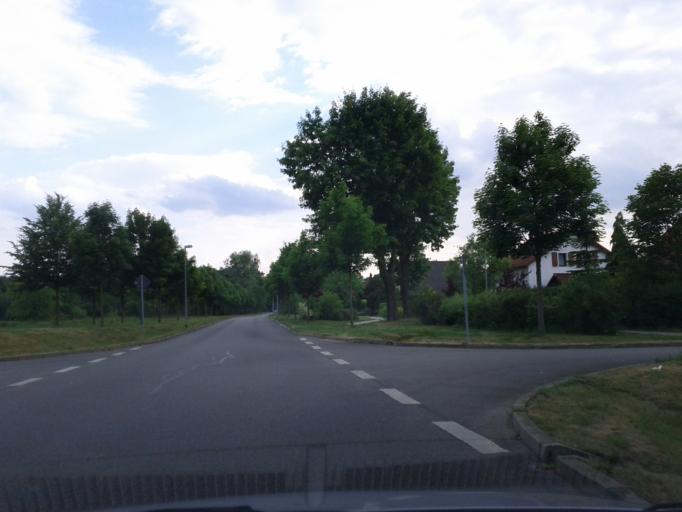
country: DE
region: Brandenburg
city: Schoneiche
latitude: 52.4683
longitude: 13.7306
